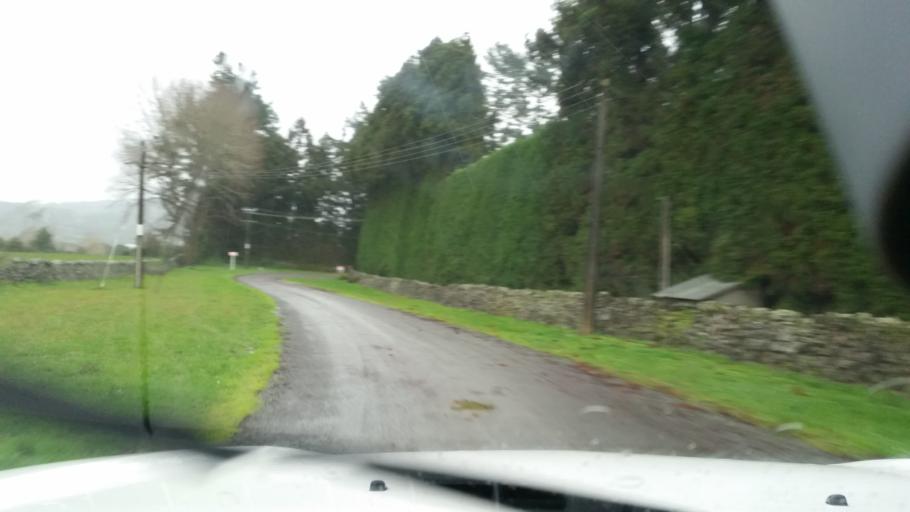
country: NZ
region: Northland
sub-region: Whangarei
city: Maungatapere
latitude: -35.7516
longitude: 174.1817
